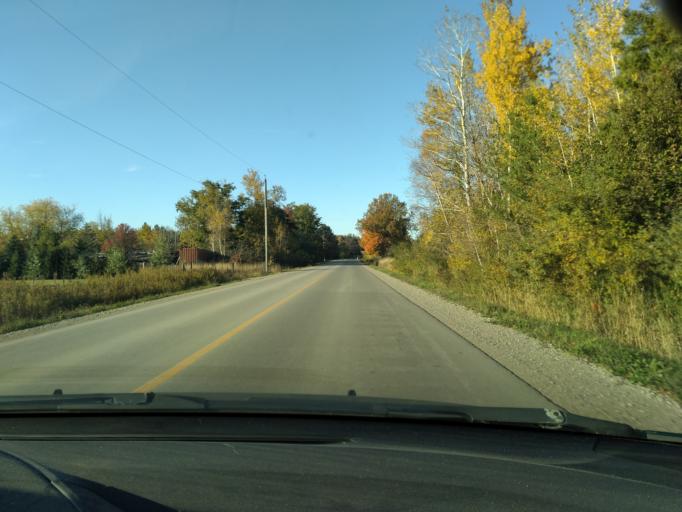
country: CA
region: Ontario
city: Bradford West Gwillimbury
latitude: 44.0515
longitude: -79.7355
